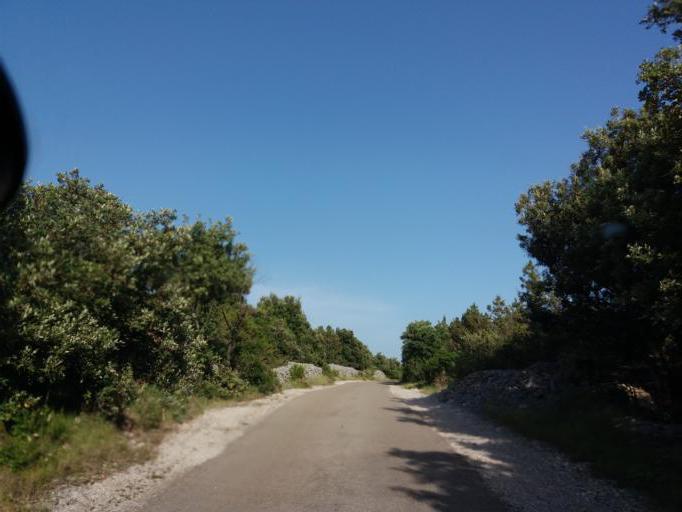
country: HR
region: Zadarska
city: Ugljan
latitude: 44.1448
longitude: 14.8388
